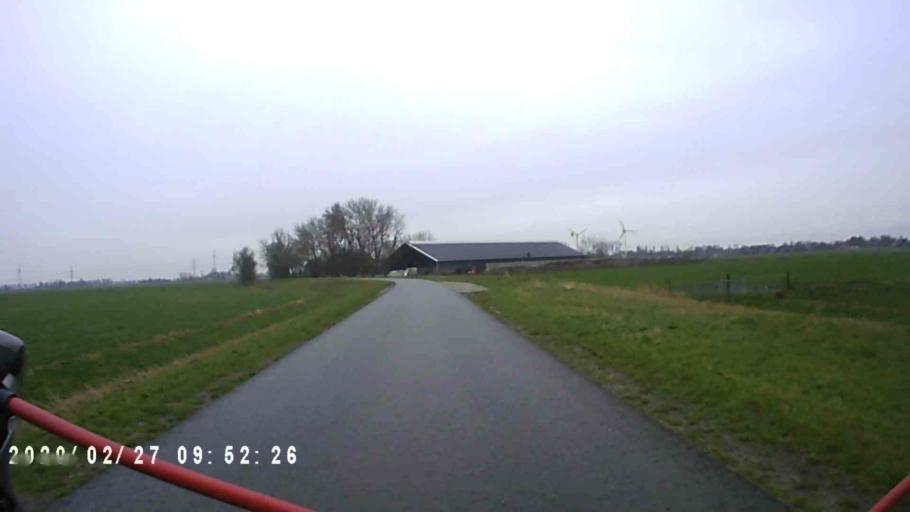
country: NL
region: Groningen
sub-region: Gemeente Zuidhorn
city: Aduard
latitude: 53.2675
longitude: 6.4601
